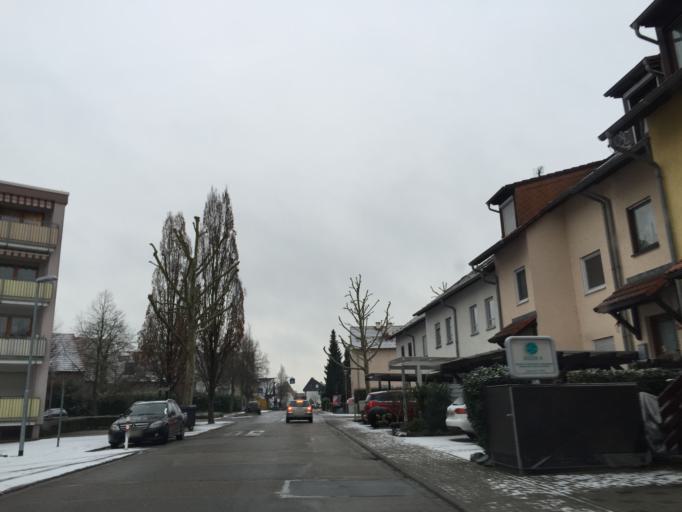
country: DE
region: Baden-Wuerttemberg
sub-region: Karlsruhe Region
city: Walldorf
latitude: 49.3031
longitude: 8.6369
